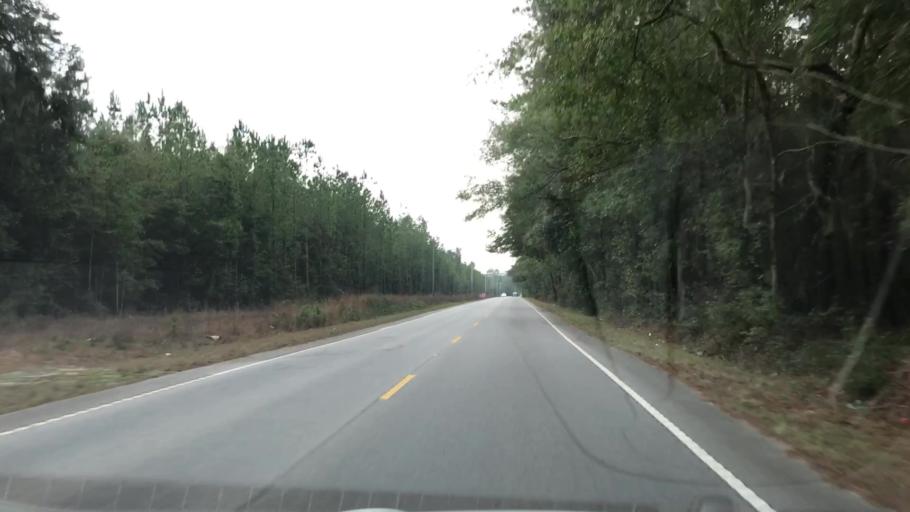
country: US
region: South Carolina
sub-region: Jasper County
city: Ridgeland
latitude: 32.5026
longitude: -80.8864
